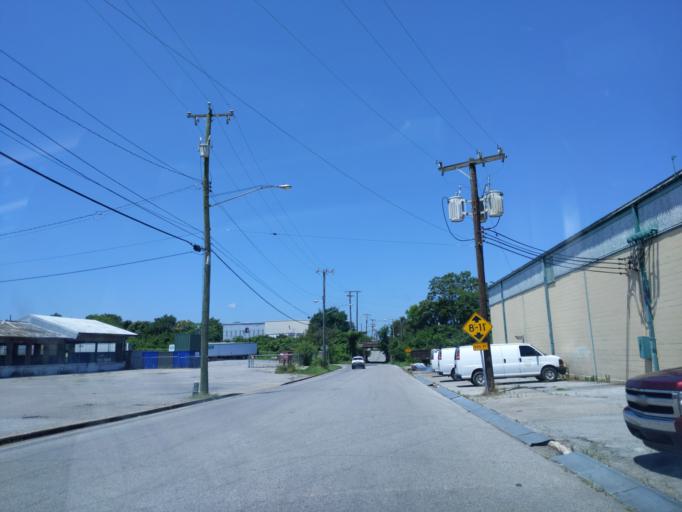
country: US
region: Tennessee
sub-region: Davidson County
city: Nashville
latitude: 36.1349
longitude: -86.7419
